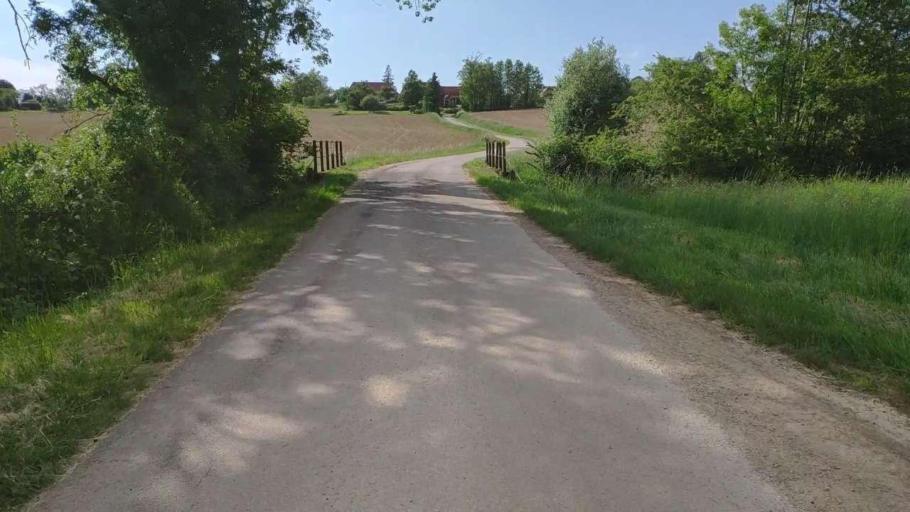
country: FR
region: Franche-Comte
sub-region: Departement du Jura
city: Bletterans
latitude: 46.8181
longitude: 5.3692
